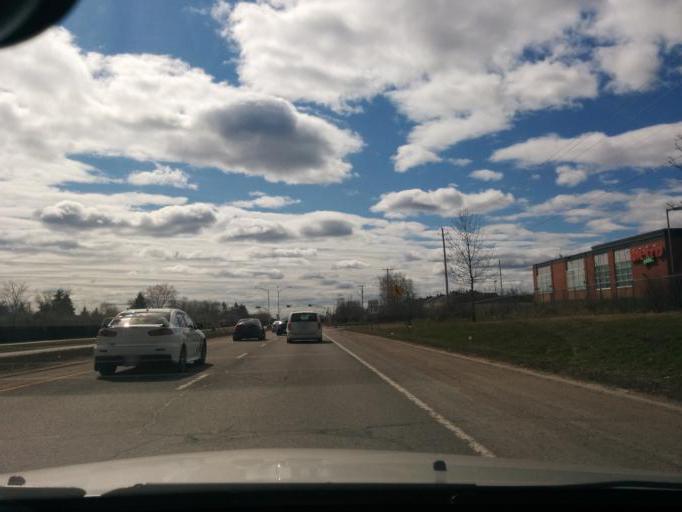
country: CA
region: Ontario
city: Bells Corners
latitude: 45.4104
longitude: -75.8410
